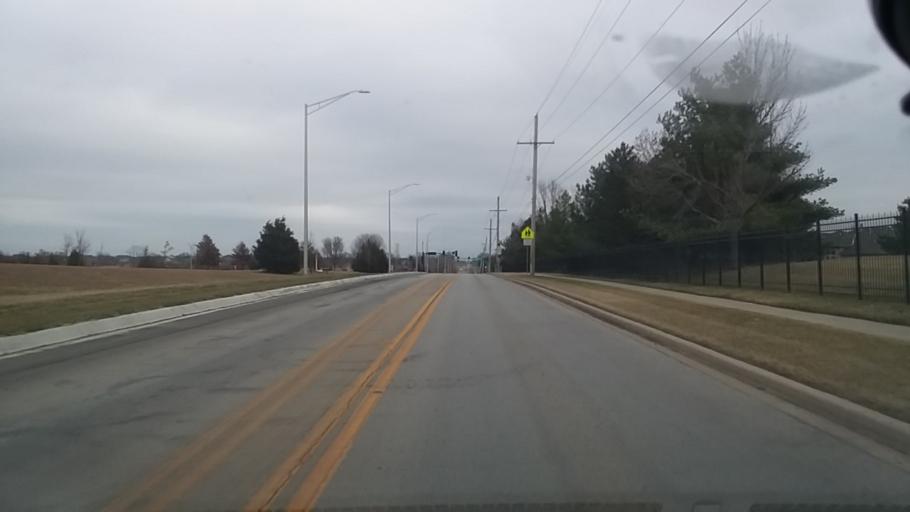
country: US
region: Kansas
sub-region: Johnson County
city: Olathe
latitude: 38.9127
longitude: -94.8429
